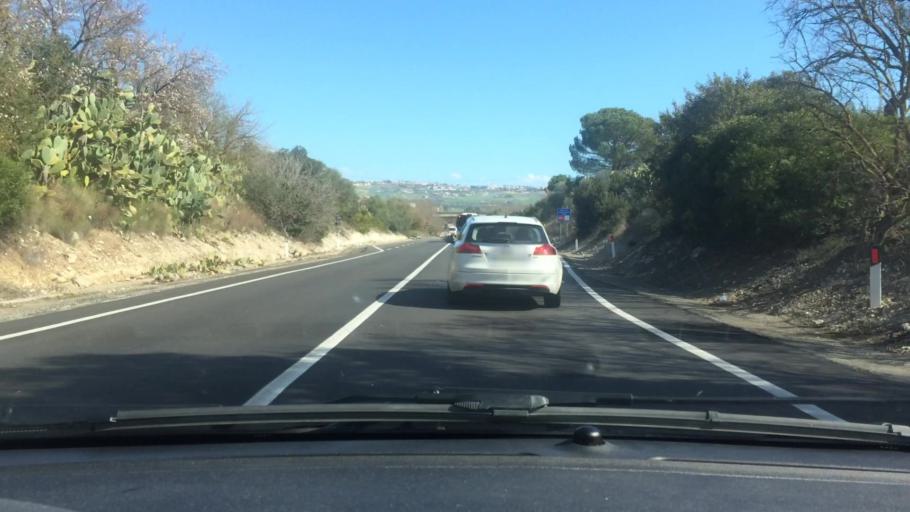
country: IT
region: Basilicate
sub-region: Provincia di Matera
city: La Martella
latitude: 40.6089
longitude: 16.5722
